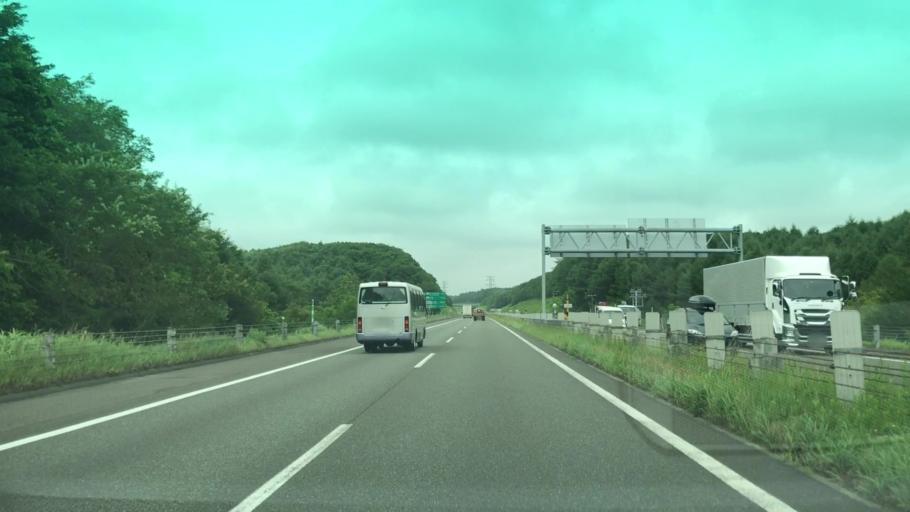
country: JP
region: Hokkaido
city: Chitose
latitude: 42.7220
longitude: 141.6528
